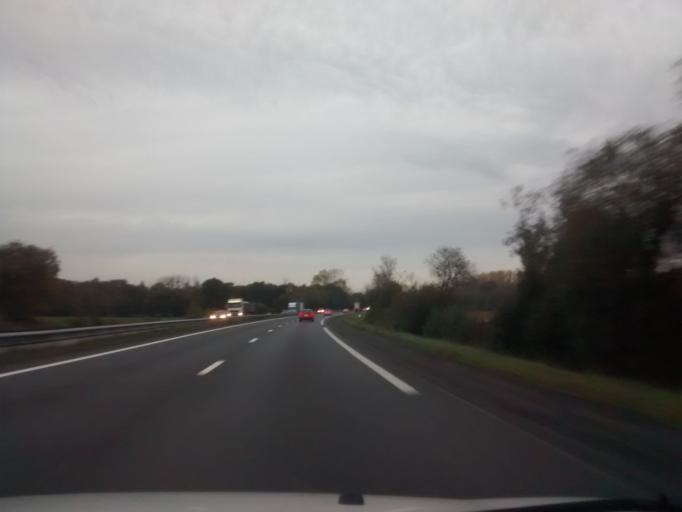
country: FR
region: Brittany
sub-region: Departement des Cotes-d'Armor
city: Broons
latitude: 48.2970
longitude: -2.2280
